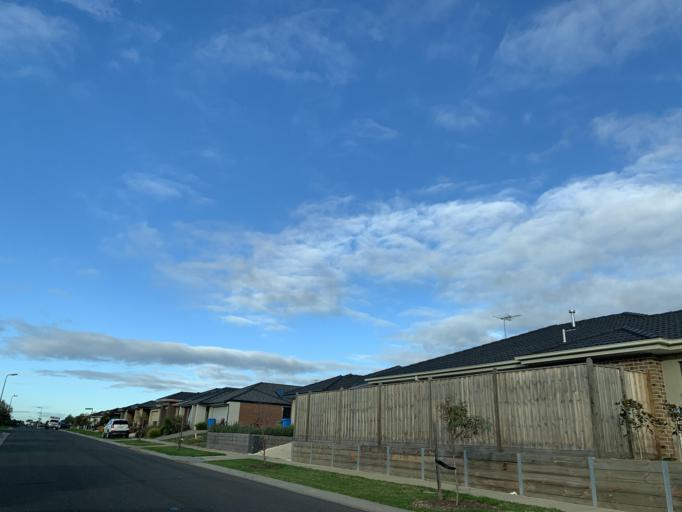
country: AU
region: Victoria
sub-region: Casey
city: Cranbourne East
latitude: -38.1257
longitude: 145.3202
